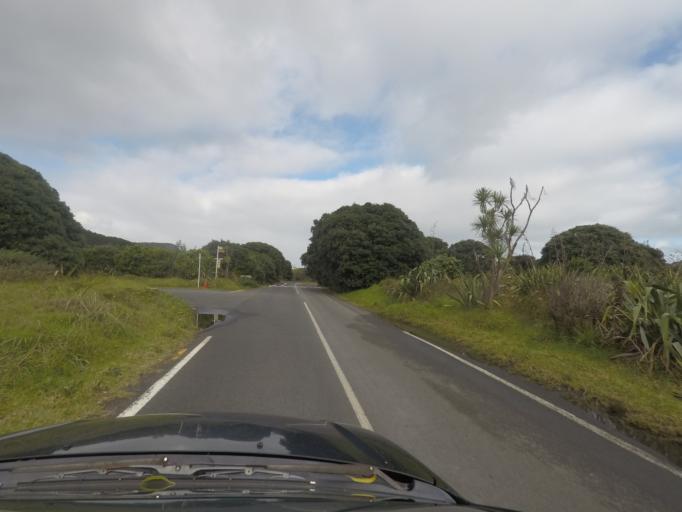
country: NZ
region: Auckland
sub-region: Auckland
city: Muriwai Beach
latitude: -36.8892
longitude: 174.4503
